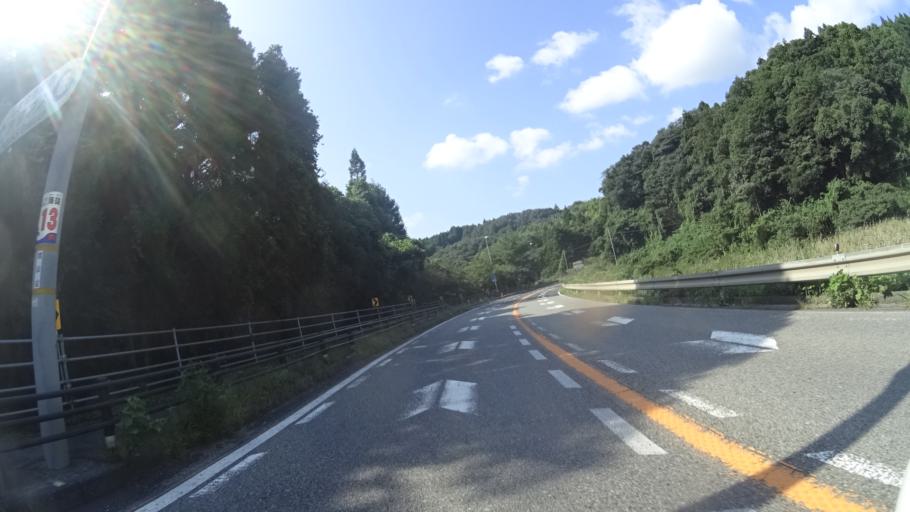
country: JP
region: Shimane
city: Gotsucho
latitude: 35.0519
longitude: 132.3129
